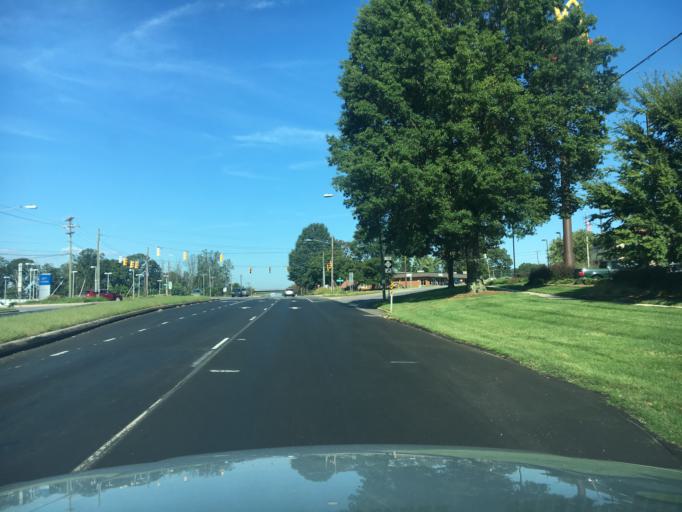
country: US
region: North Carolina
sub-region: Catawba County
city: Hickory
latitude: 35.7151
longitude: -81.3363
